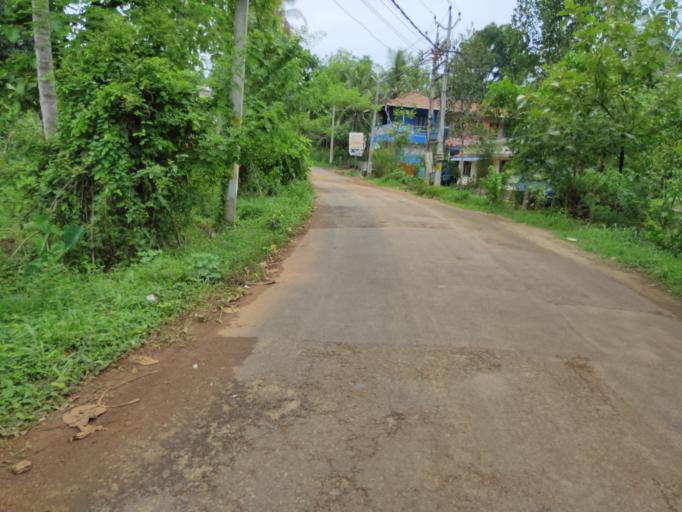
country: IN
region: Kerala
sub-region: Malappuram
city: Manjeri
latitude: 11.2474
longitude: 76.2486
